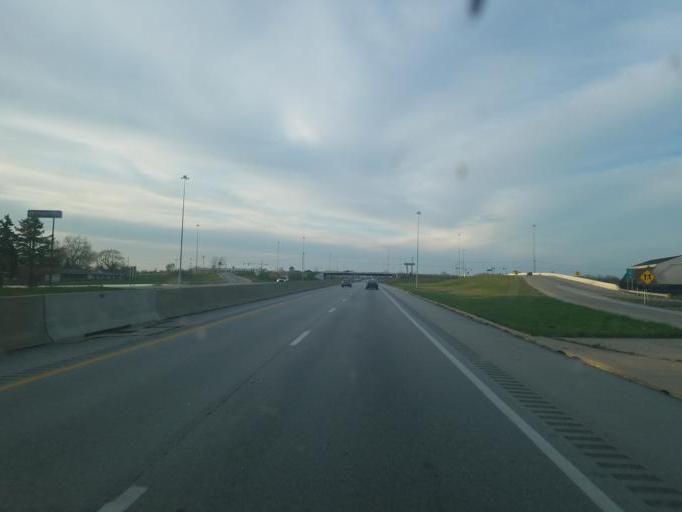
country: US
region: Ohio
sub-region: Wood County
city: Northwood
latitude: 41.6126
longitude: -83.4769
